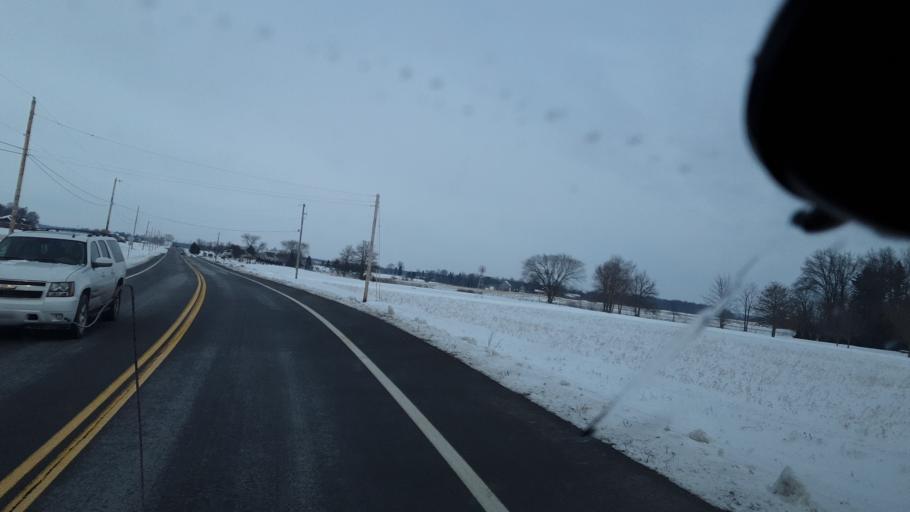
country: US
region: Ohio
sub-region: Union County
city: Marysville
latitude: 40.1865
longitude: -83.3361
